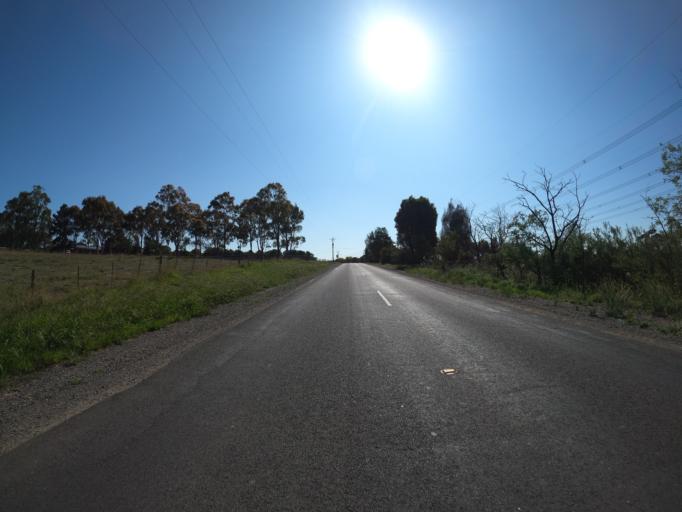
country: AU
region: Victoria
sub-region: Hume
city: Greenvale
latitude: -37.5471
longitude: 144.8732
